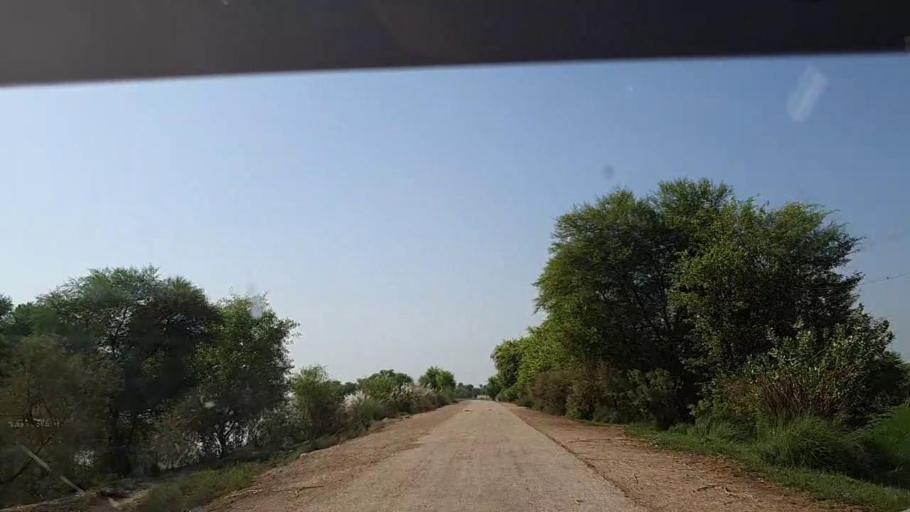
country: PK
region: Sindh
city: Ghauspur
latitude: 28.1914
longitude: 69.0564
